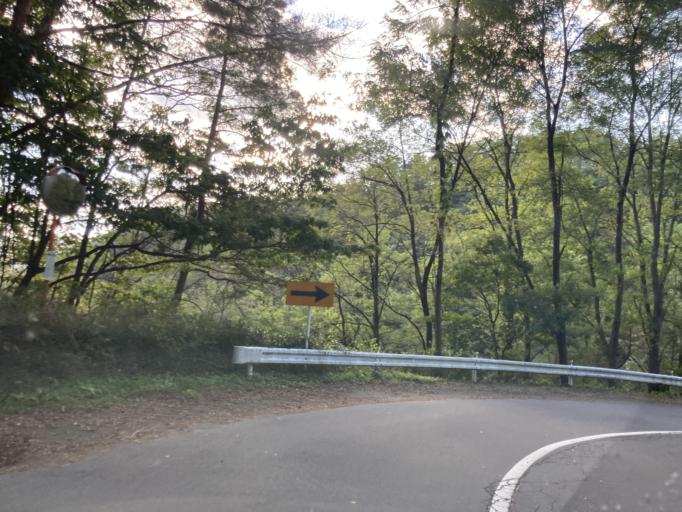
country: JP
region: Nagano
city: Ueda
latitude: 36.4009
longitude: 138.1026
